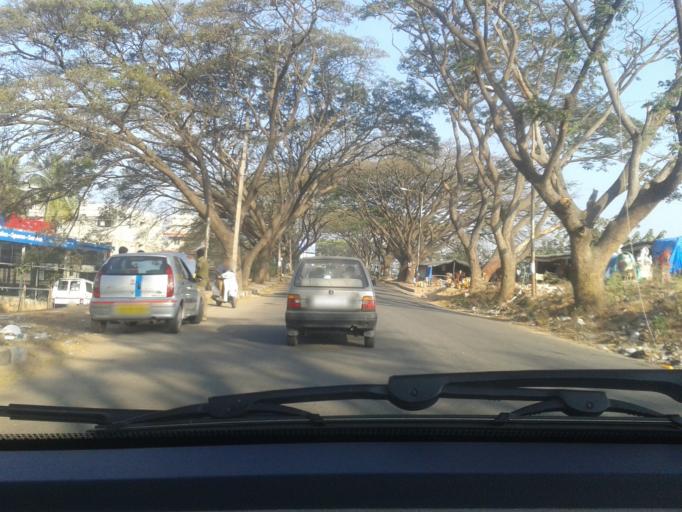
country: IN
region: Karnataka
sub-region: Bangalore Urban
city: Yelahanka
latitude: 13.0405
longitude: 77.5632
